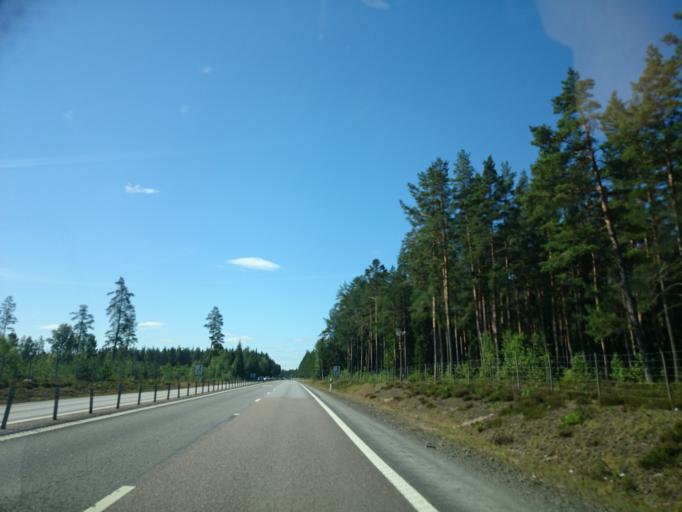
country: SE
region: Gaevleborg
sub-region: Gavle Kommun
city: Norrsundet
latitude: 61.0620
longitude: 16.9630
